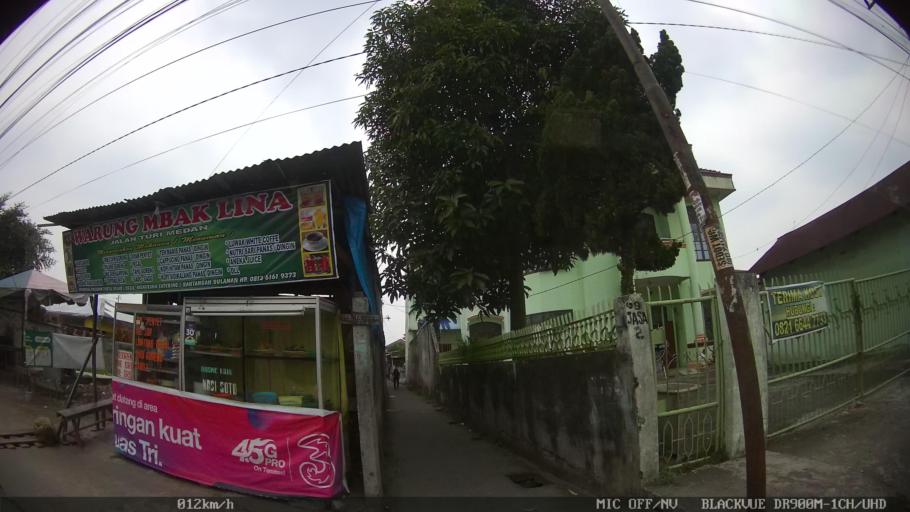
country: ID
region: North Sumatra
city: Medan
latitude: 3.5628
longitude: 98.6969
